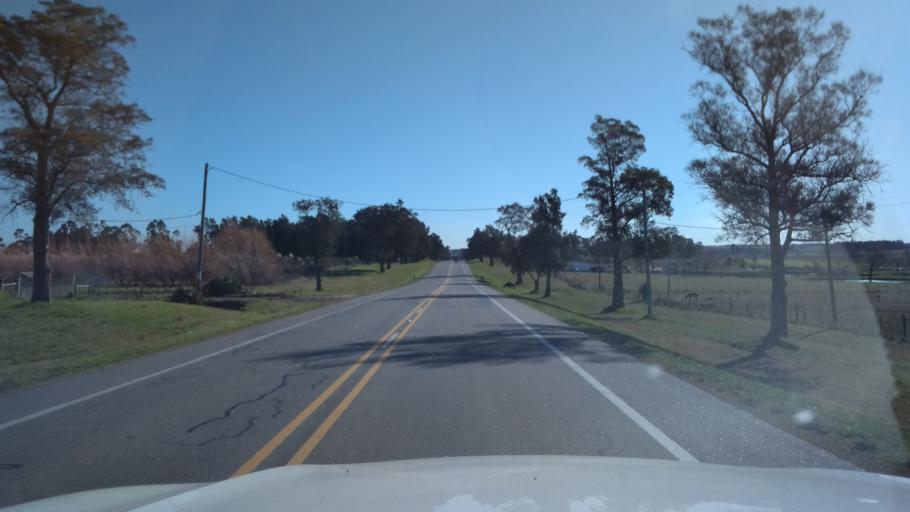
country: UY
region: Canelones
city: San Jacinto
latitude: -34.5389
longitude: -55.9021
